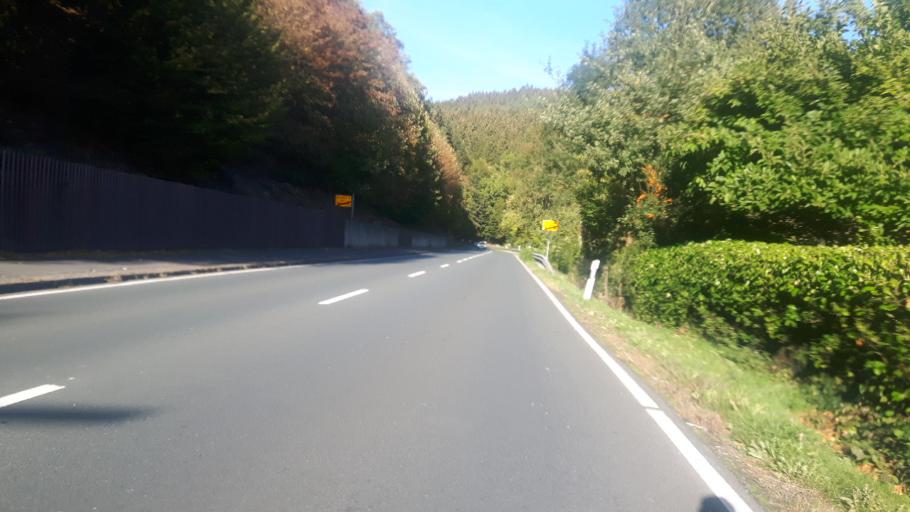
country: DE
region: Rheinland-Pfalz
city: Wallmenroth
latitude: 50.8002
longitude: 7.8486
